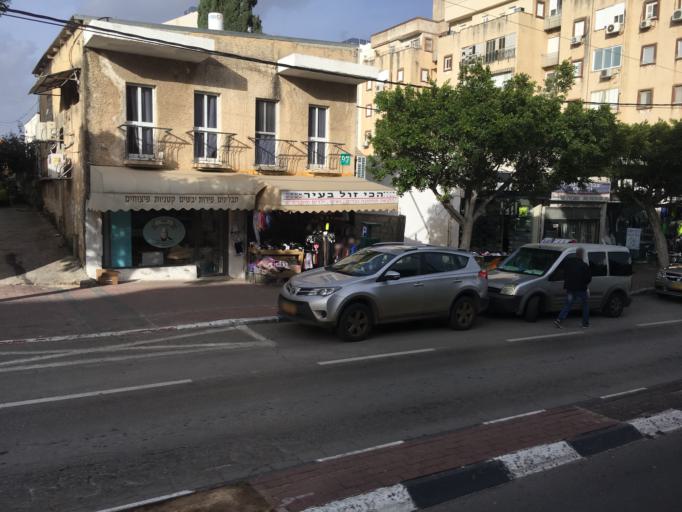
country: IL
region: Central District
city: Kfar Saba
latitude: 32.1756
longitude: 34.9071
